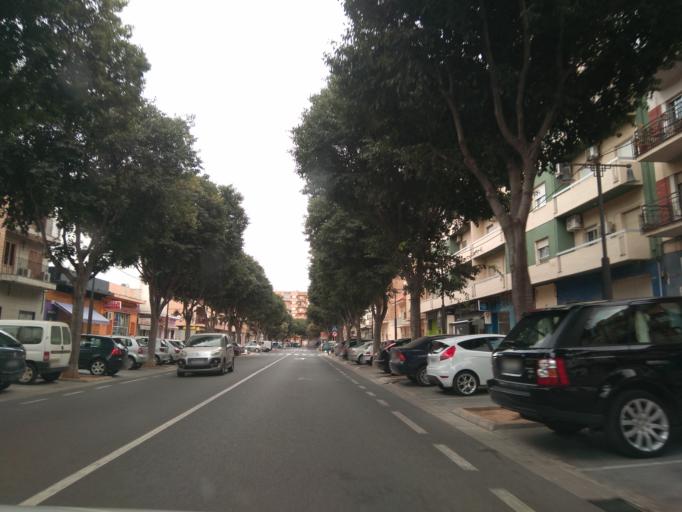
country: ES
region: Valencia
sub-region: Provincia de Valencia
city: L'Alcudia
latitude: 39.1969
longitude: -0.5035
